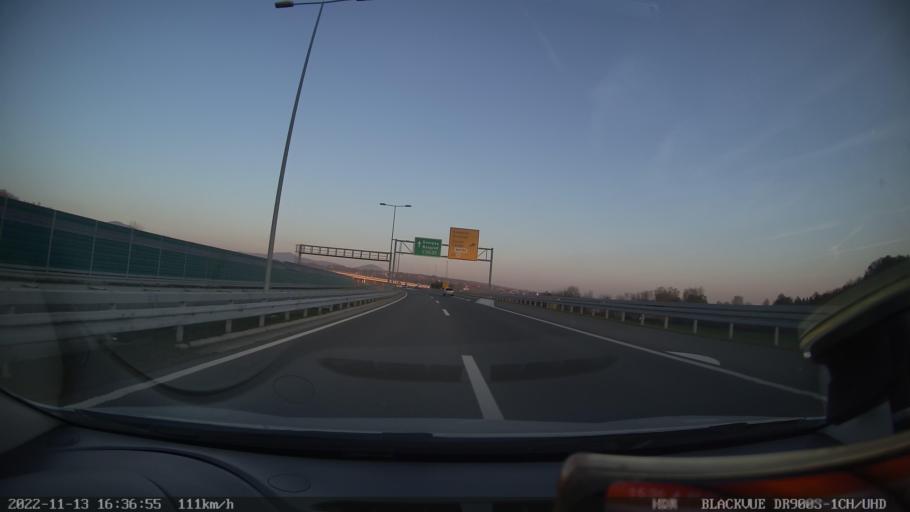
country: RS
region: Central Serbia
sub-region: Moravicki Okrug
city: Cacak
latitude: 43.9197
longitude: 20.3884
